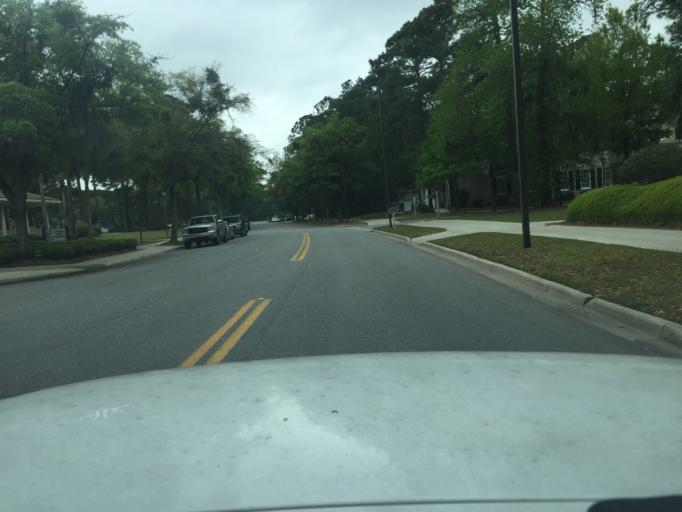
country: US
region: Georgia
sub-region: Chatham County
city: Skidaway Island
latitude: 31.9406
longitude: -81.0526
